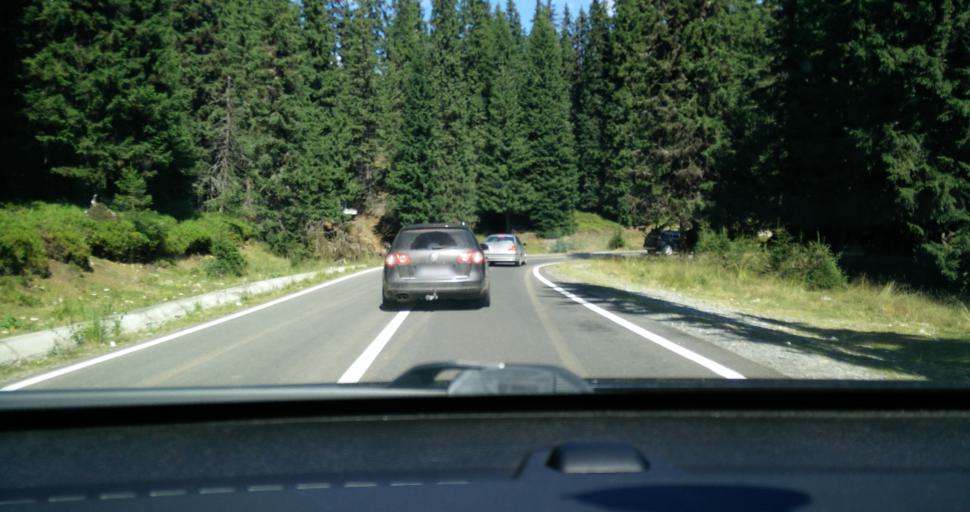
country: RO
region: Hunedoara
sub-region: Oras Petrila
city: Petrila
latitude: 45.4718
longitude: 23.6326
